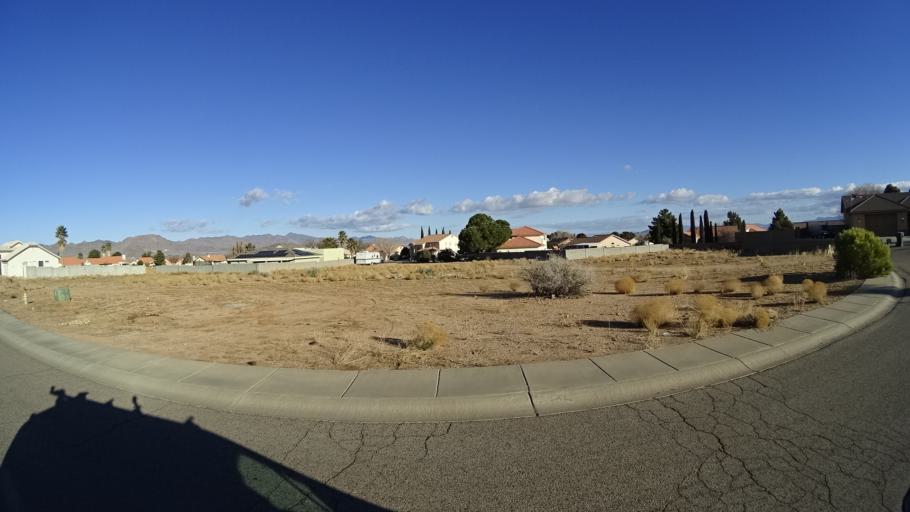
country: US
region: Arizona
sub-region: Mohave County
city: New Kingman-Butler
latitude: 35.2211
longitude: -113.9732
